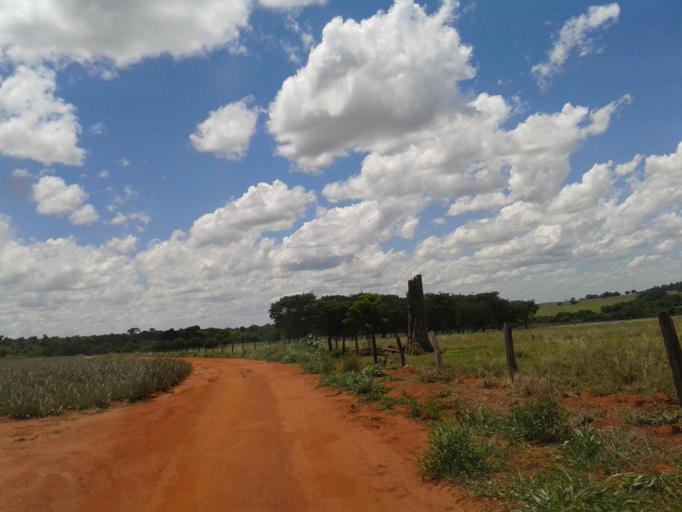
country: BR
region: Minas Gerais
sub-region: Centralina
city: Centralina
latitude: -18.6940
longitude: -49.1599
